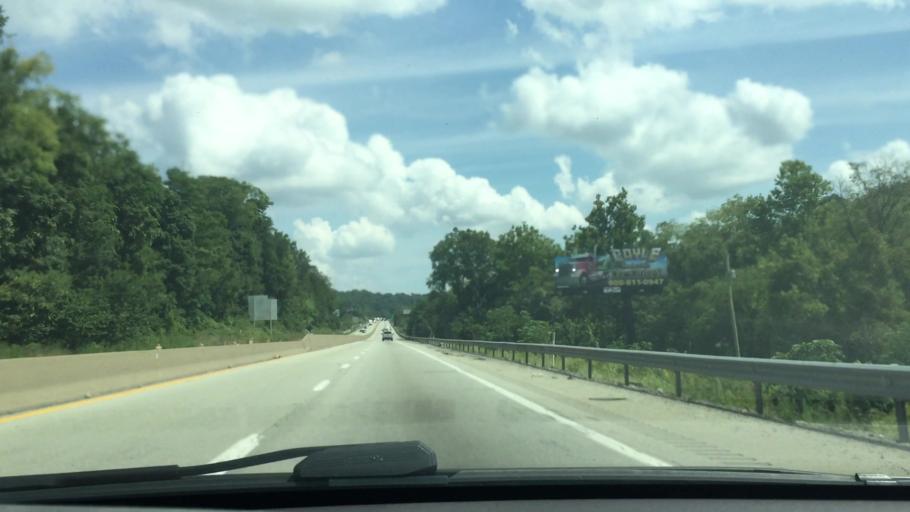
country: US
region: Pennsylvania
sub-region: Washington County
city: Bentleyville
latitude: 40.1301
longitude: -79.9849
